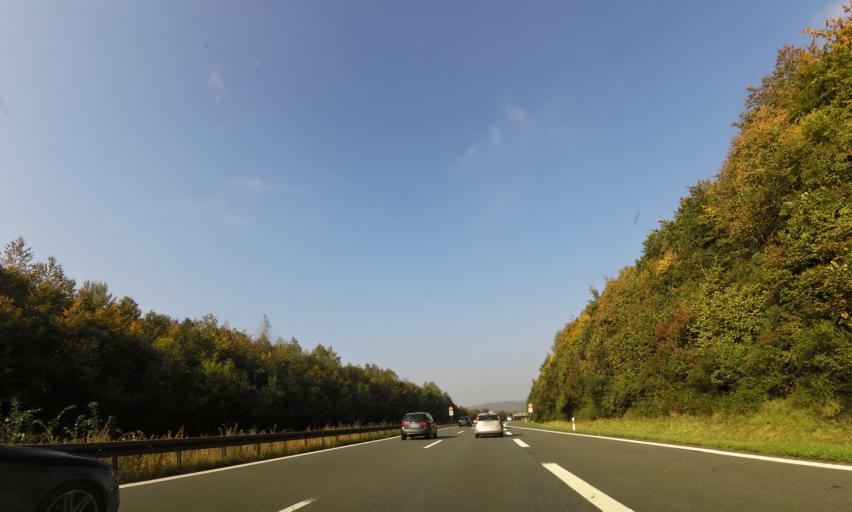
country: DE
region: Bavaria
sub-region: Regierungsbezirk Mittelfranken
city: Schnelldorf
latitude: 49.2053
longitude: 10.1948
